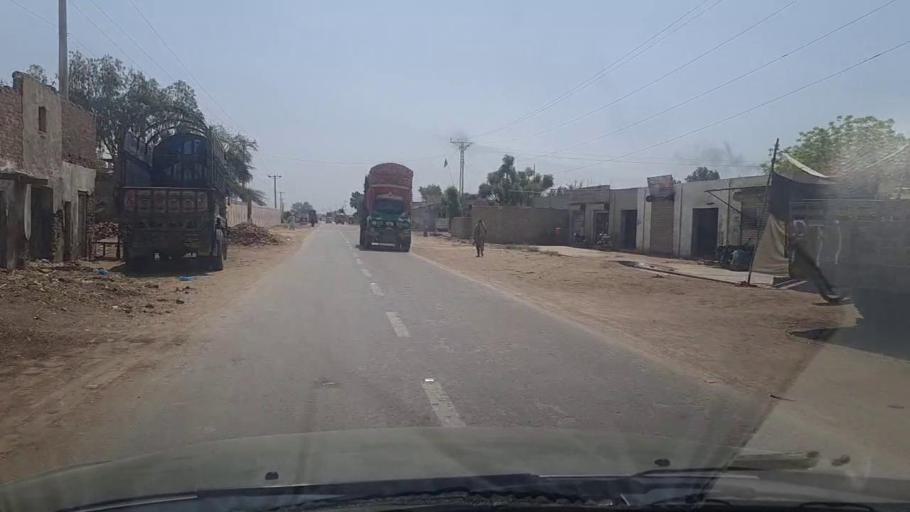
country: PK
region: Sindh
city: Hyderabad
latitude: 25.3858
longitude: 68.4332
